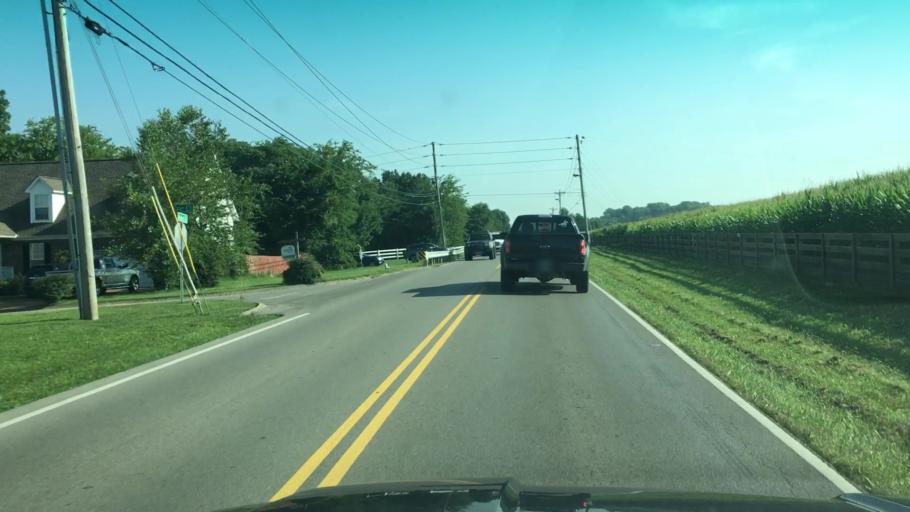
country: US
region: Tennessee
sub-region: Williamson County
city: Thompson's Station
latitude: 35.7793
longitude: -86.8793
